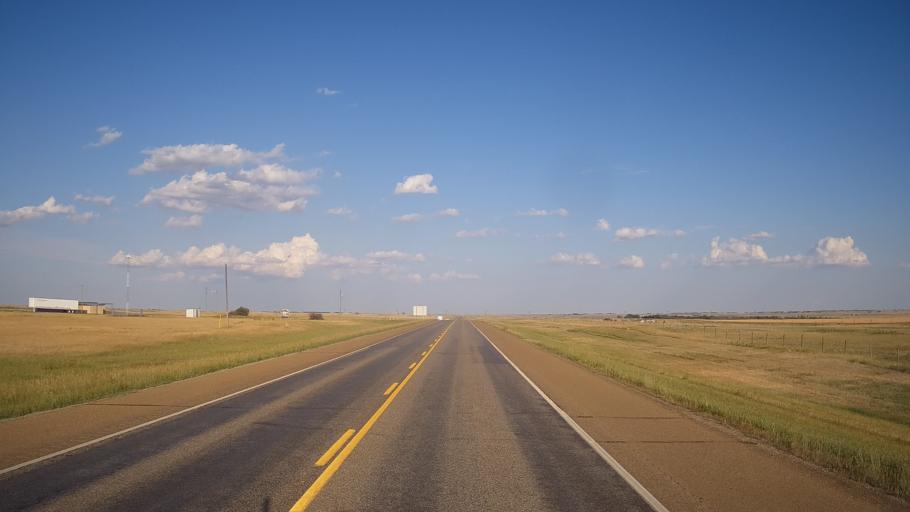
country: CA
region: Alberta
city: Hanna
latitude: 51.6281
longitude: -111.9035
